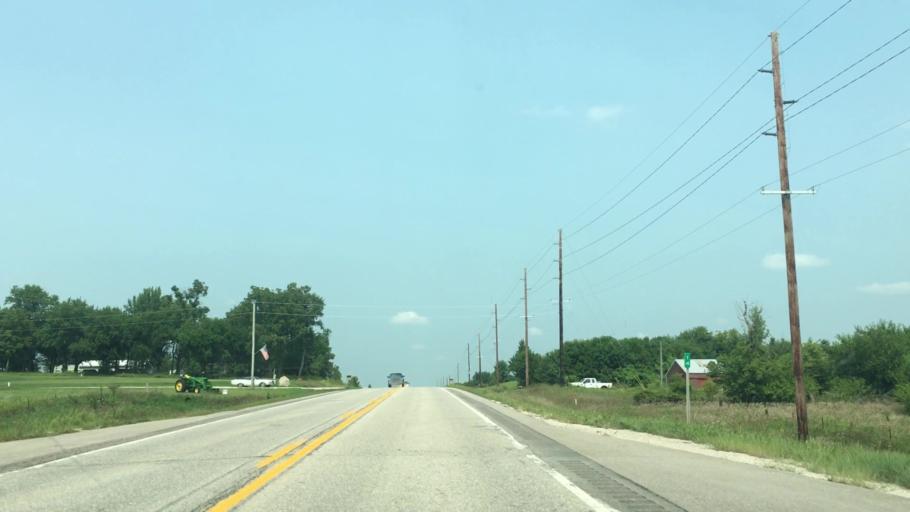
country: US
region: Iowa
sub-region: Benton County
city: Urbana
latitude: 42.2613
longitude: -91.8906
